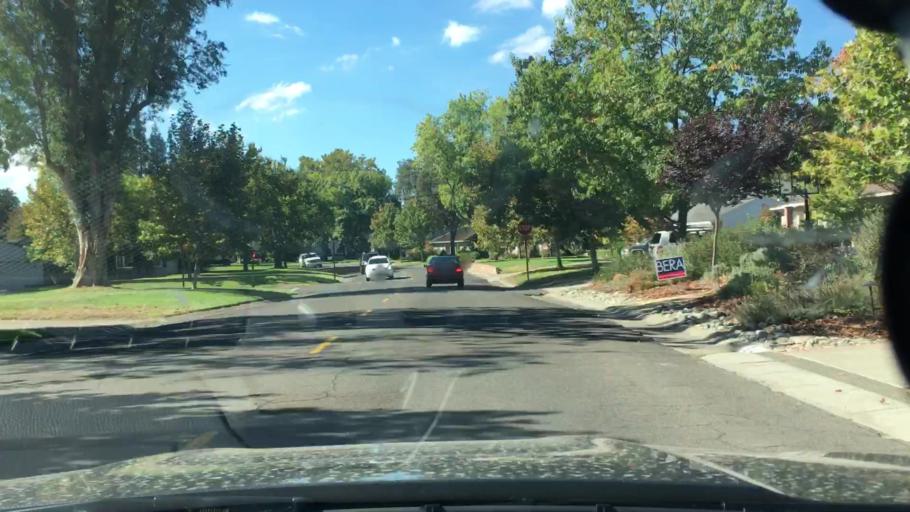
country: US
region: California
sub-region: Sacramento County
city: Arden-Arcade
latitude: 38.5800
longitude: -121.3790
